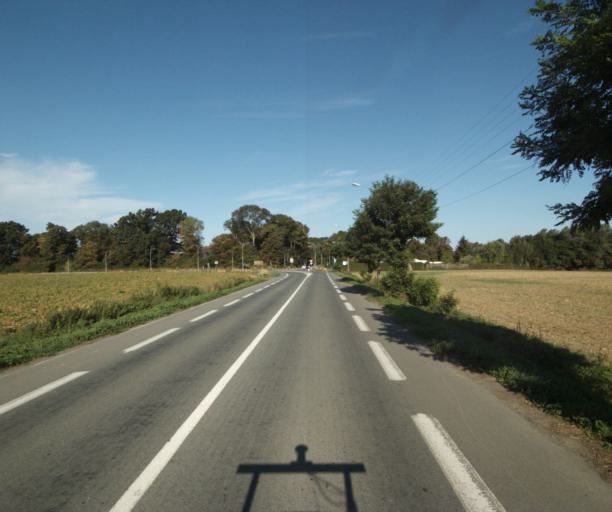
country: FR
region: Nord-Pas-de-Calais
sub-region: Departement du Nord
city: Cysoing
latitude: 50.5765
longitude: 3.1957
